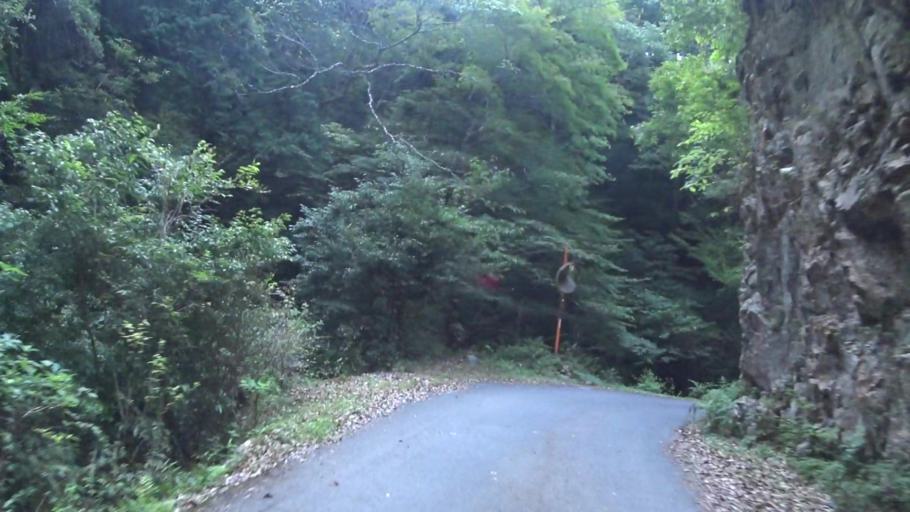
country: JP
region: Fukui
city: Obama
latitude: 35.2890
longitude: 135.6461
